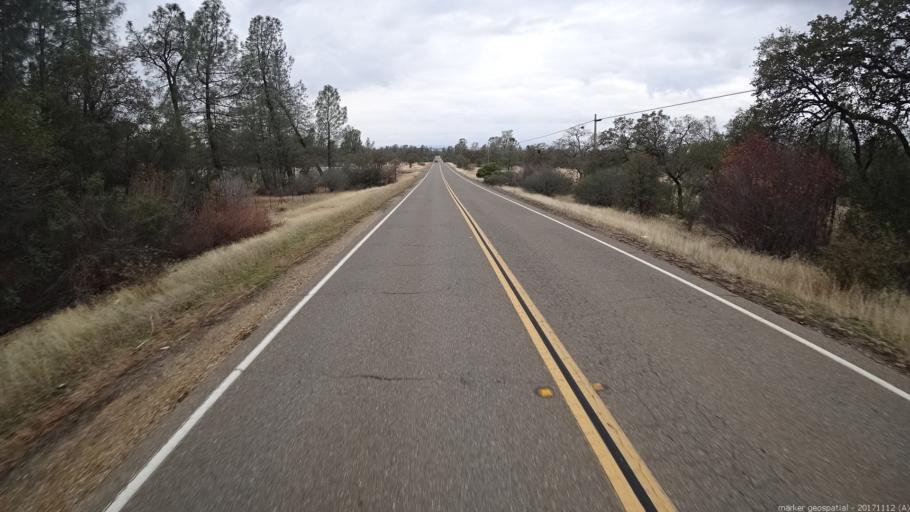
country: US
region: California
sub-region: Shasta County
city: Palo Cedro
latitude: 40.4811
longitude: -122.0913
